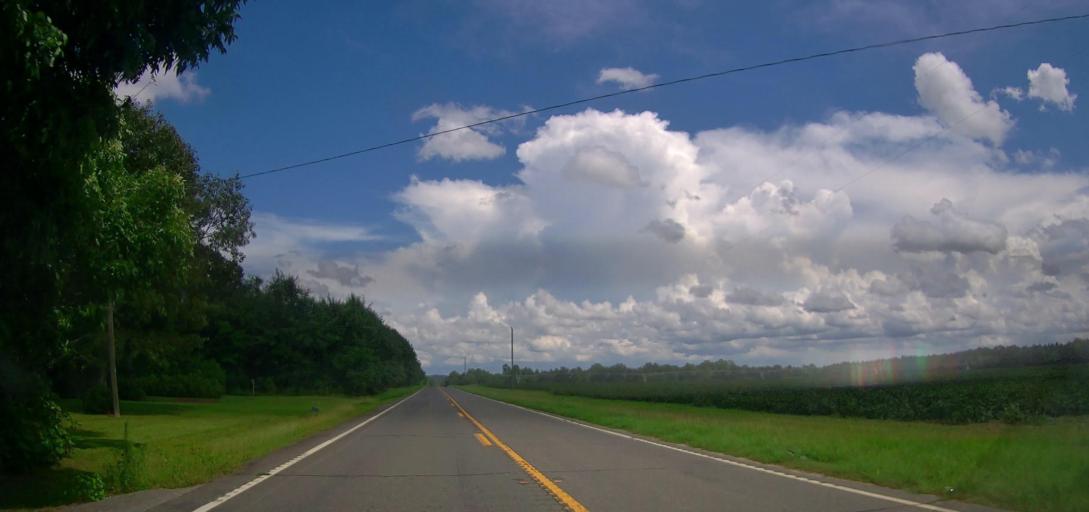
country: US
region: Georgia
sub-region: Macon County
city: Marshallville
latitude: 32.4334
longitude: -84.0655
